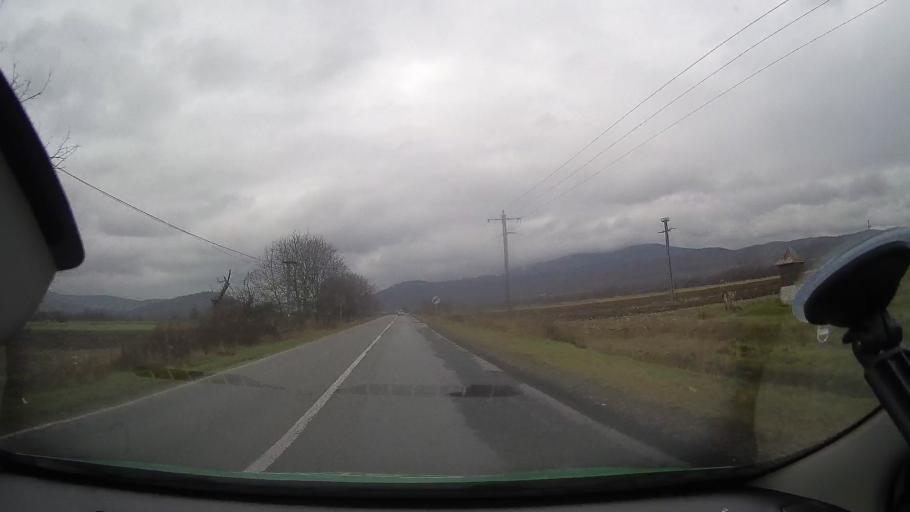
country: RO
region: Arad
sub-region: Comuna Buteni
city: Buteni
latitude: 46.3204
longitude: 22.1309
